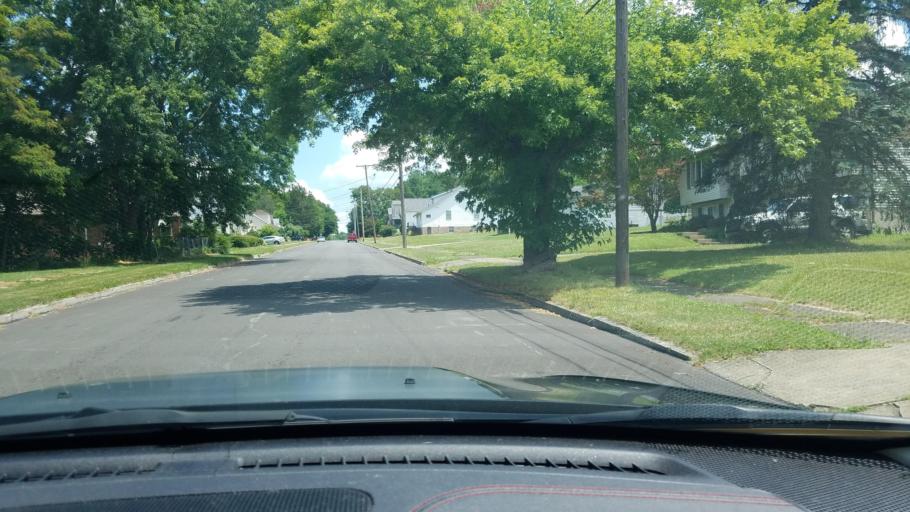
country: US
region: Ohio
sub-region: Mahoning County
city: Campbell
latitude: 41.0775
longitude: -80.5864
